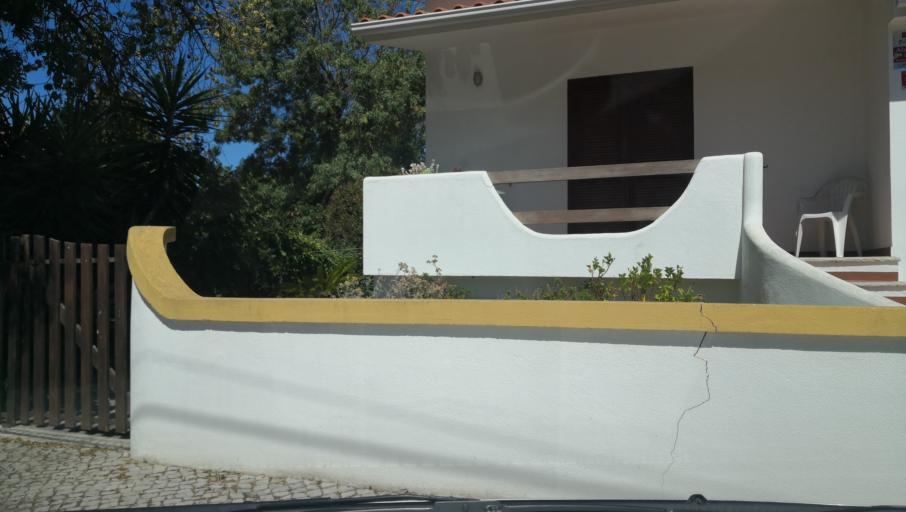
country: PT
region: Setubal
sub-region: Setubal
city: Setubal
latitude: 38.5342
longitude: -8.9035
